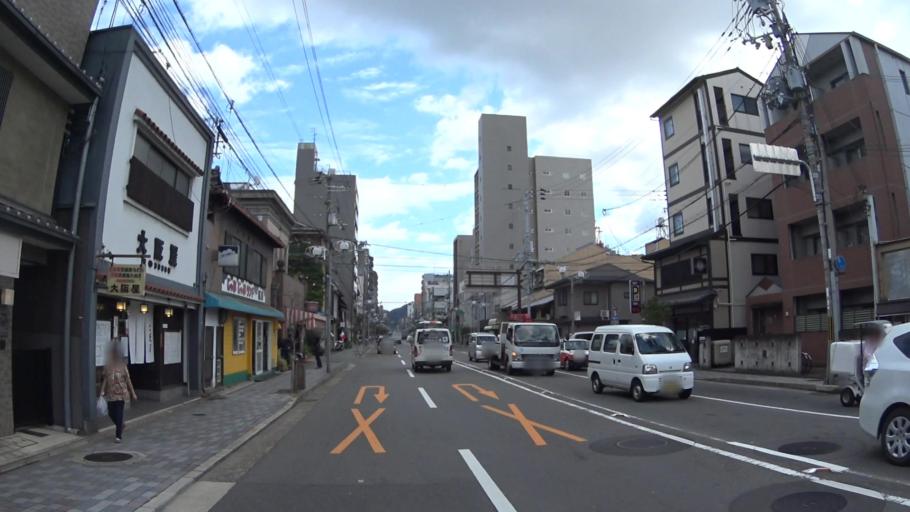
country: JP
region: Kyoto
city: Kyoto
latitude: 34.9893
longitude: 135.7533
